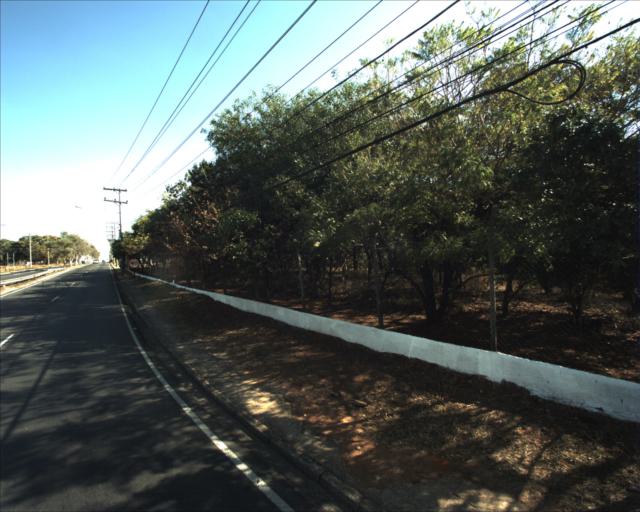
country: BR
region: Sao Paulo
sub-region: Sorocaba
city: Sorocaba
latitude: -23.4557
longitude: -47.4187
